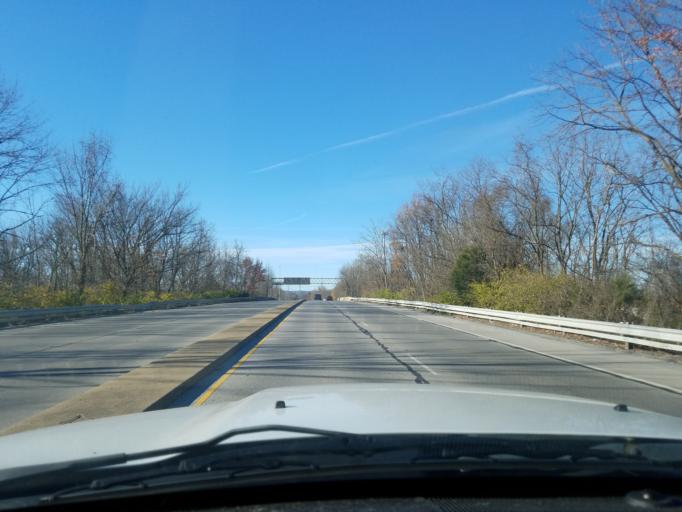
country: US
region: Indiana
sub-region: Clark County
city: Clarksville
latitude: 38.2984
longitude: -85.7743
